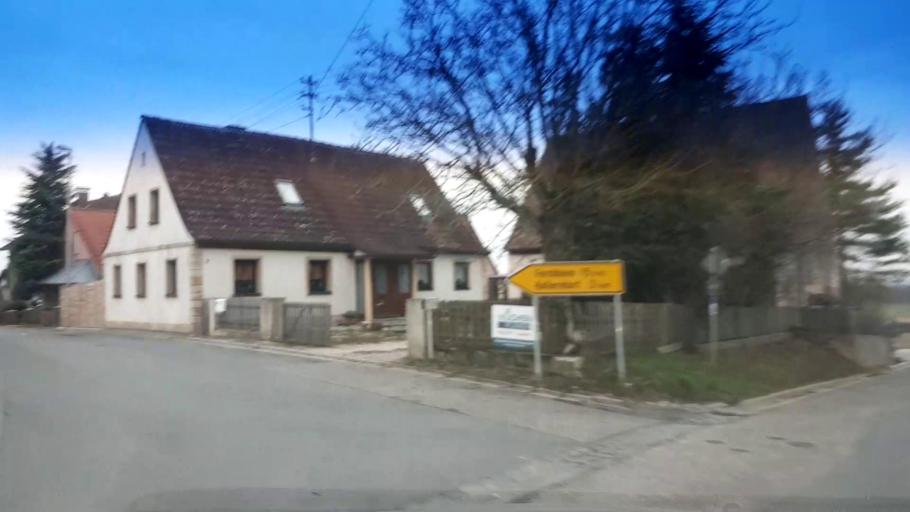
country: DE
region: Bavaria
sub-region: Upper Franconia
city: Hallerndorf
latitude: 49.7692
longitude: 10.9486
